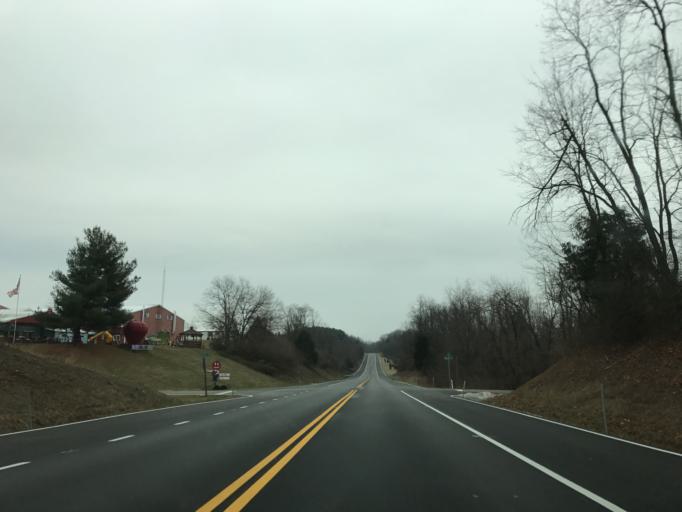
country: US
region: Maryland
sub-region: Carroll County
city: Westminster
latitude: 39.6020
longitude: -77.0515
